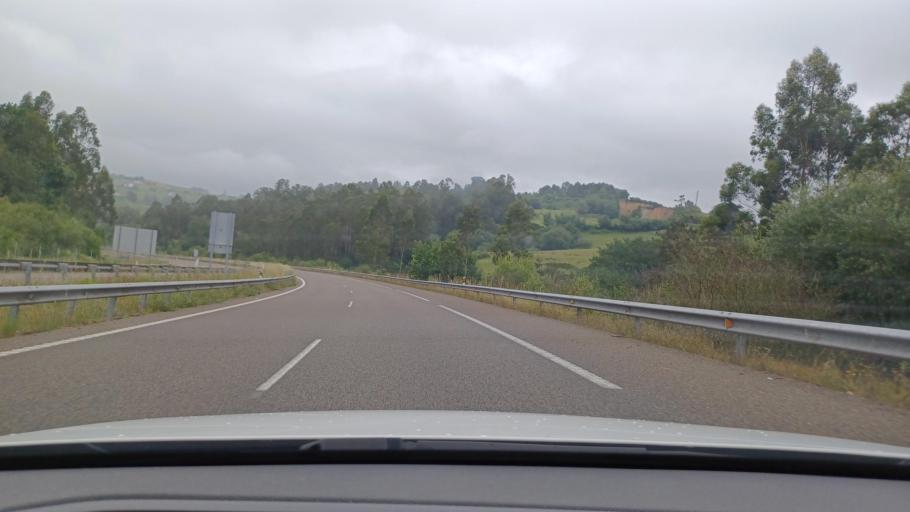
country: ES
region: Asturias
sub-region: Province of Asturias
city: Lugones
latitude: 43.4658
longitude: -5.7598
